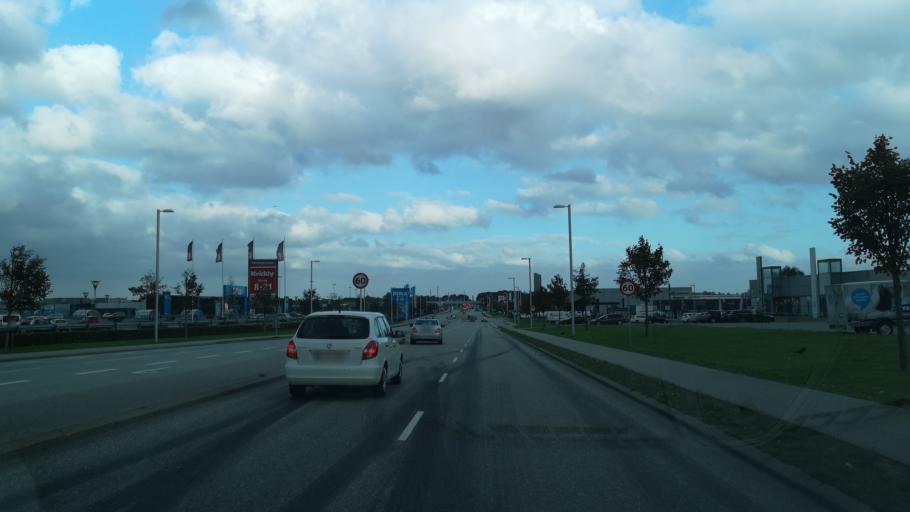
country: DK
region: Central Jutland
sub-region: Herning Kommune
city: Herning
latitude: 56.1346
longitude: 9.0002
